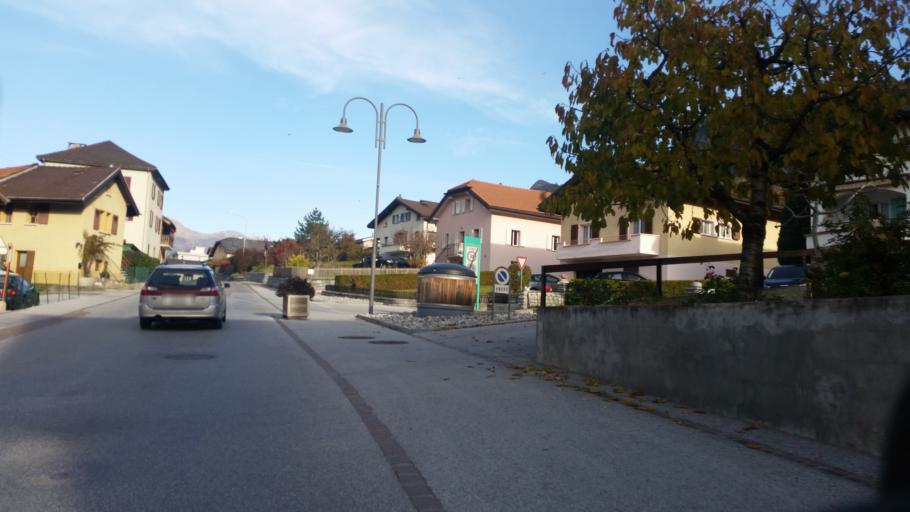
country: CH
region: Valais
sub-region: Sierre District
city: Chalais
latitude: 46.2619
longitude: 7.4969
